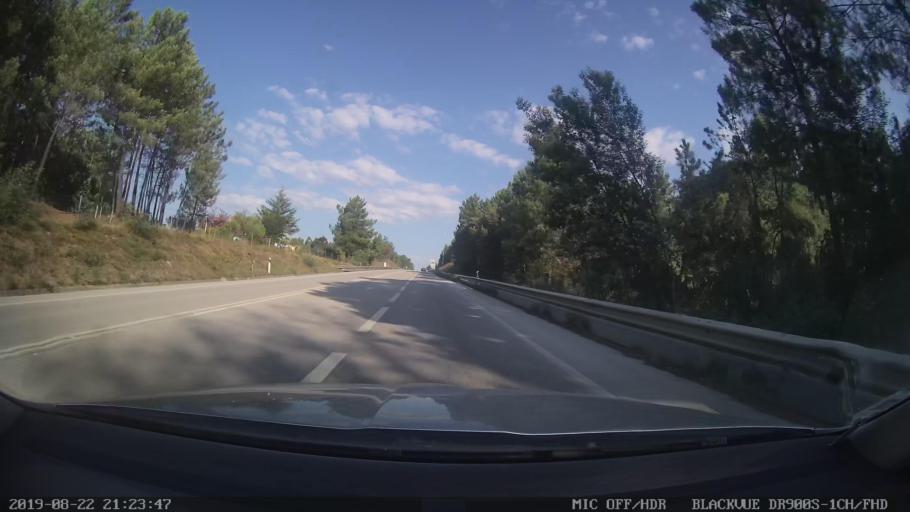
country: PT
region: Castelo Branco
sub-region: Serta
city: Serta
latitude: 39.8352
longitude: -8.1125
